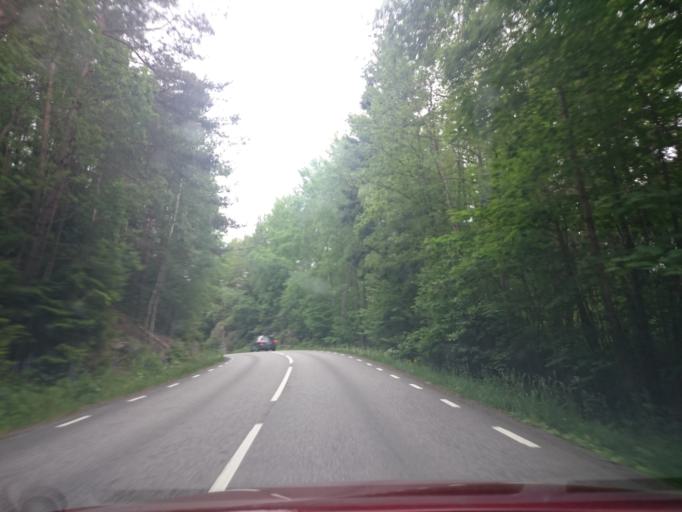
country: SE
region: Vaestra Goetaland
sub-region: Lerums Kommun
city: Stenkullen
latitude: 57.7461
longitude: 12.3310
